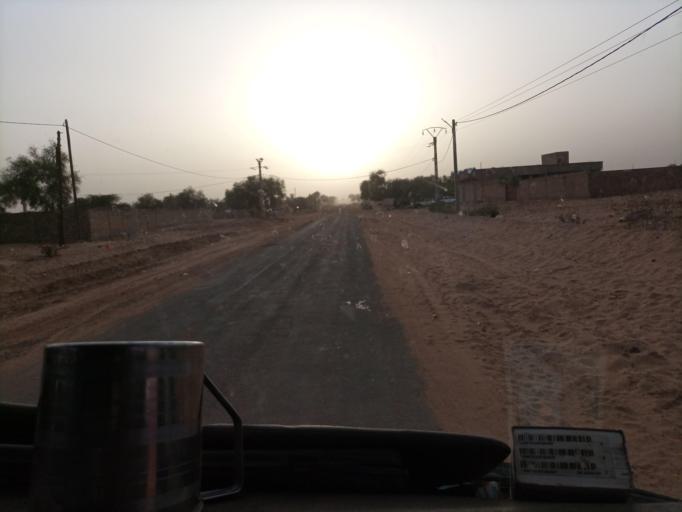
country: SN
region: Louga
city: Dara
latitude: 15.4028
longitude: -15.6592
